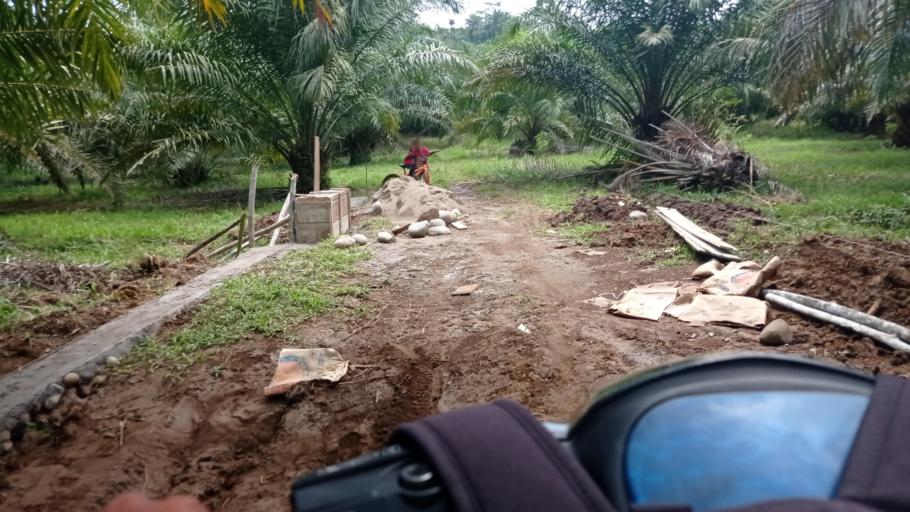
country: ID
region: Jambi
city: Sungai Penuh
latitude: -2.4869
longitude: 101.2283
